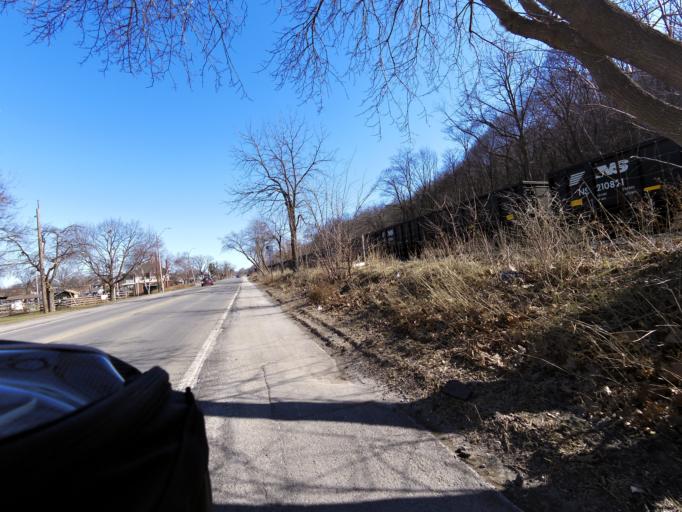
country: CA
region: Ontario
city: Hamilton
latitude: 43.2386
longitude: -79.8311
